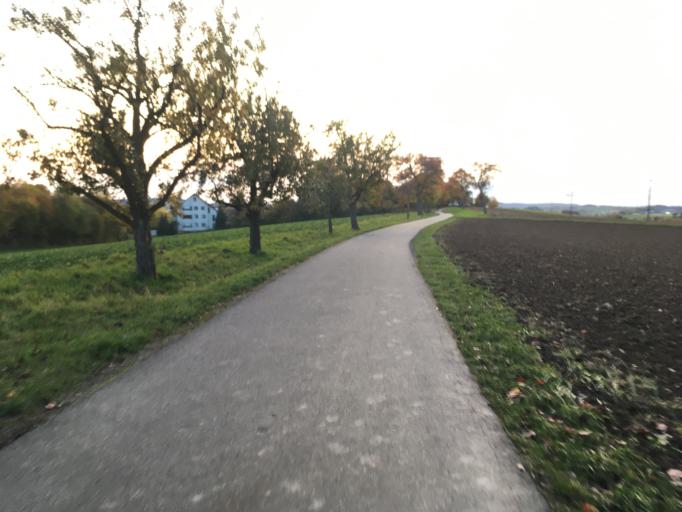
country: DE
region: Baden-Wuerttemberg
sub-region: Regierungsbezirk Stuttgart
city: Ohringen
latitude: 49.2109
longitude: 9.5211
